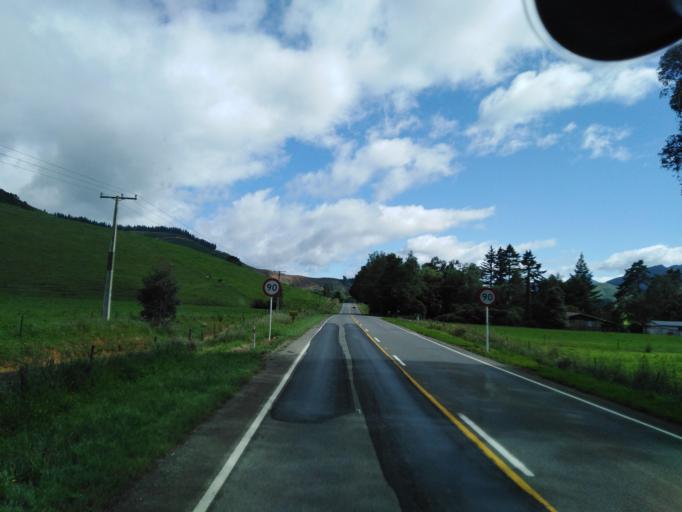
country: NZ
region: Nelson
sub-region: Nelson City
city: Nelson
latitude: -41.2765
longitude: 173.5732
